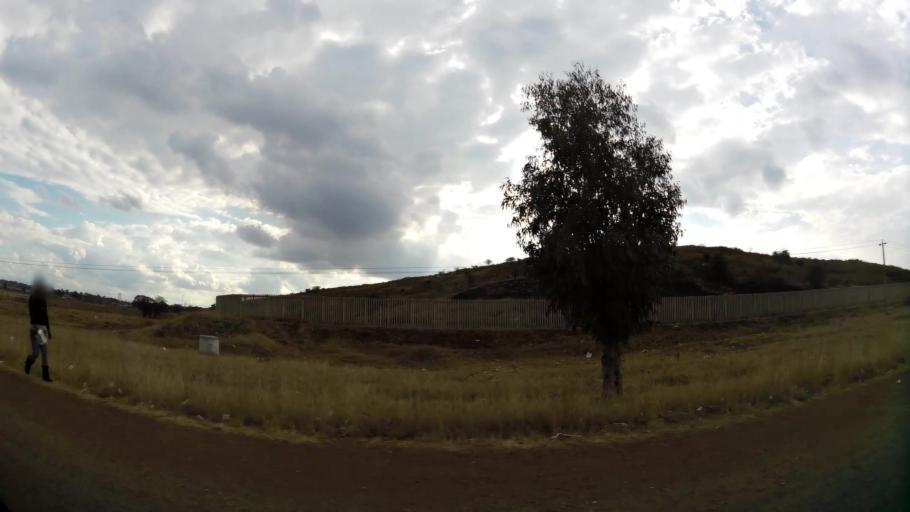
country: ZA
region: Gauteng
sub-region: Sedibeng District Municipality
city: Vanderbijlpark
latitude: -26.6704
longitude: 27.8614
